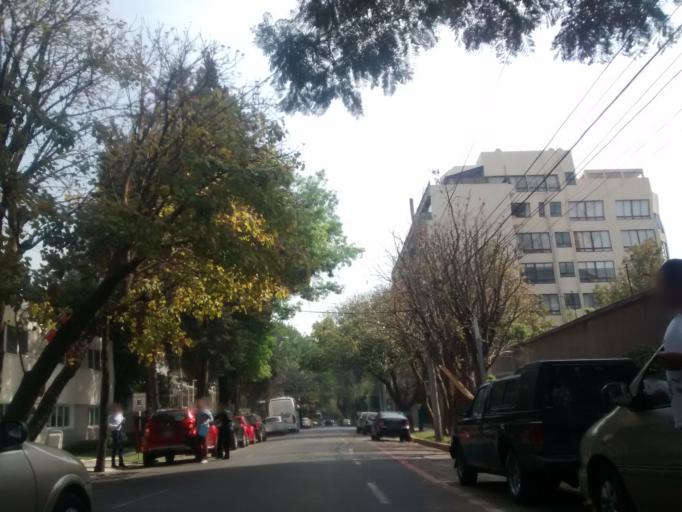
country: MX
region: Mexico City
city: Miguel Hidalgo
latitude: 19.4287
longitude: -99.1888
